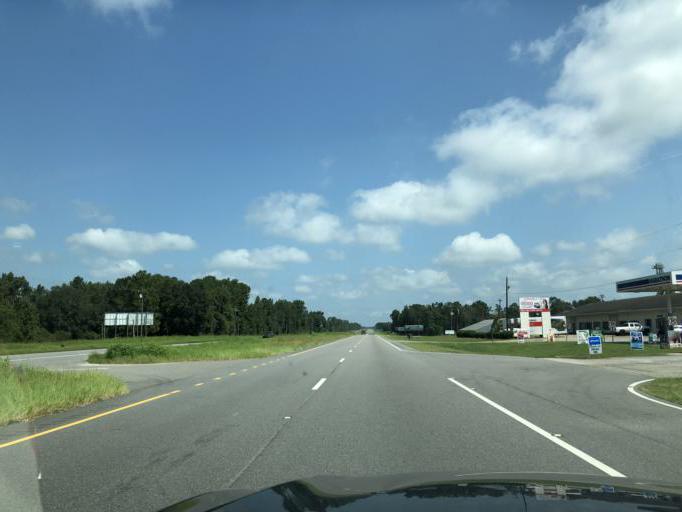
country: US
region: Alabama
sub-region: Houston County
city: Cottonwood
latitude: 31.0196
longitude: -85.4073
